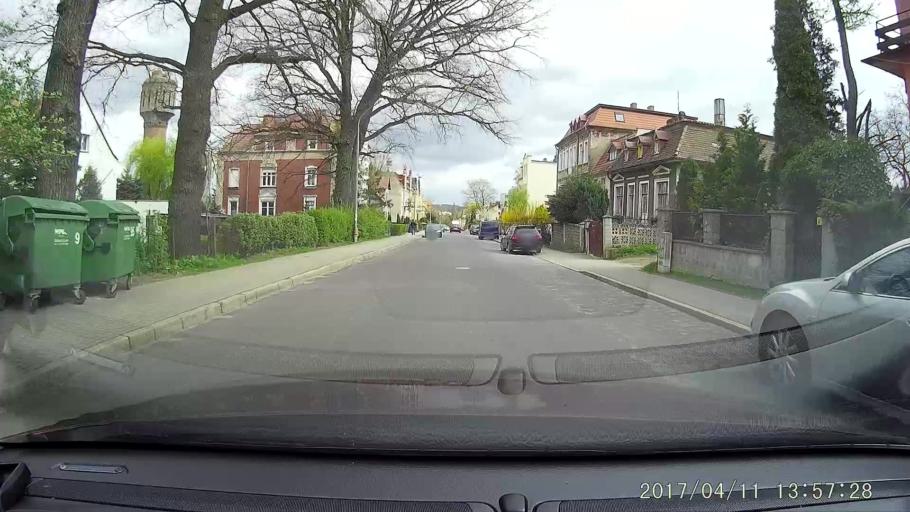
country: PL
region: Lower Silesian Voivodeship
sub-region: Powiat zgorzelecki
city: Zgorzelec
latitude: 51.1386
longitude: 15.0067
